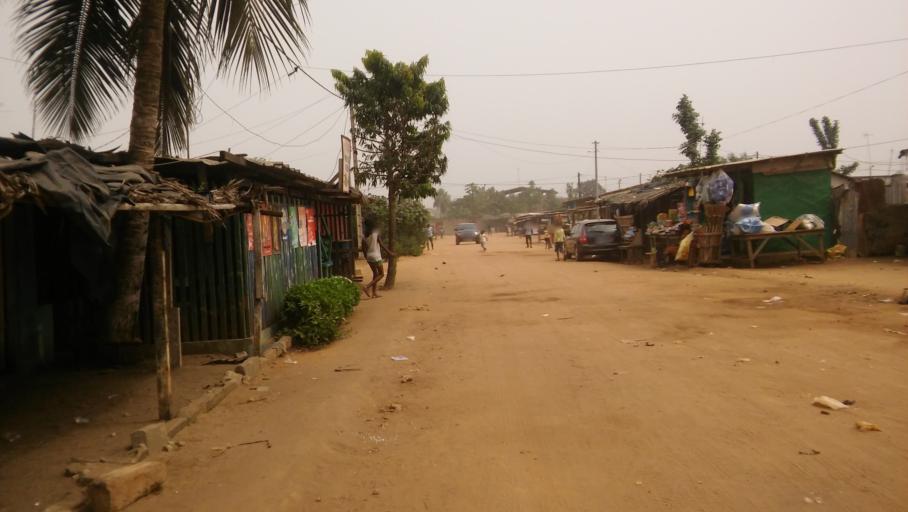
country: CI
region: Sud-Comoe
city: Grand-Bassam
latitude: 5.2144
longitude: -3.7354
